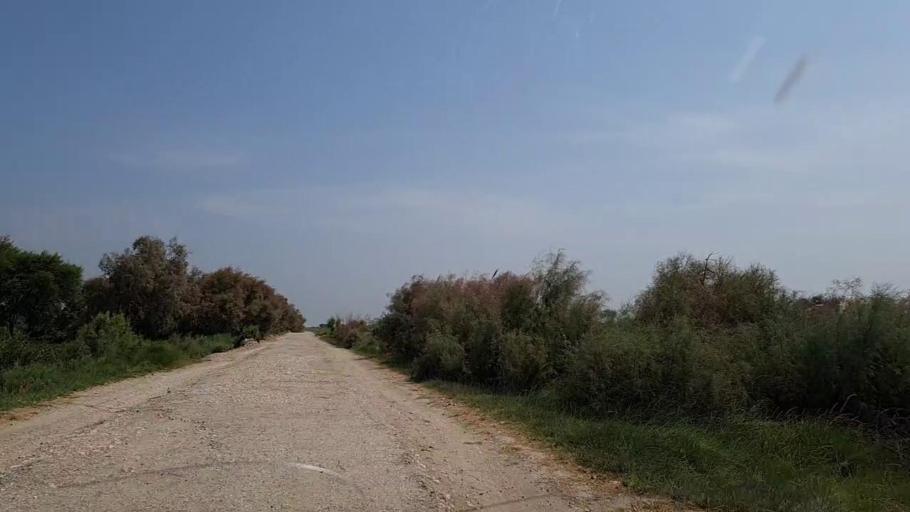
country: PK
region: Sindh
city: Khanpur
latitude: 27.8126
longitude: 69.3077
